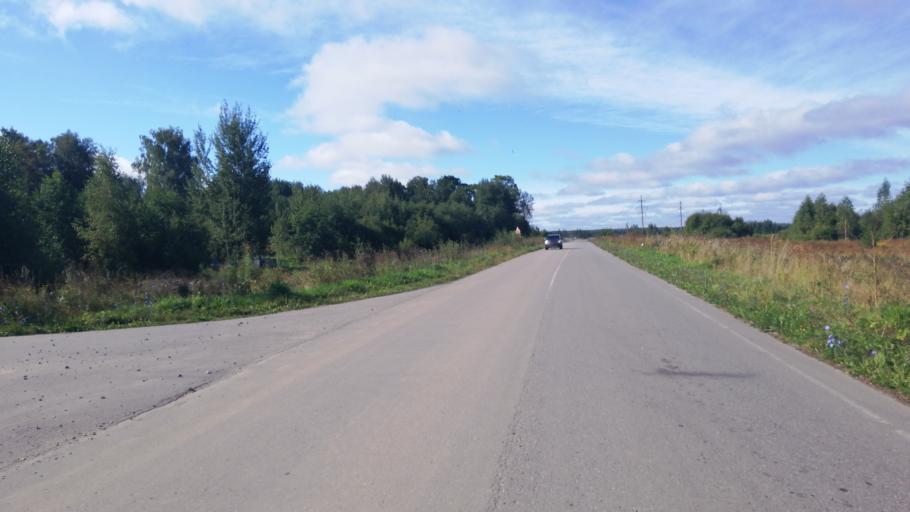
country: RU
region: Ivanovo
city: Novo-Talitsy
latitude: 57.0163
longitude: 40.7568
